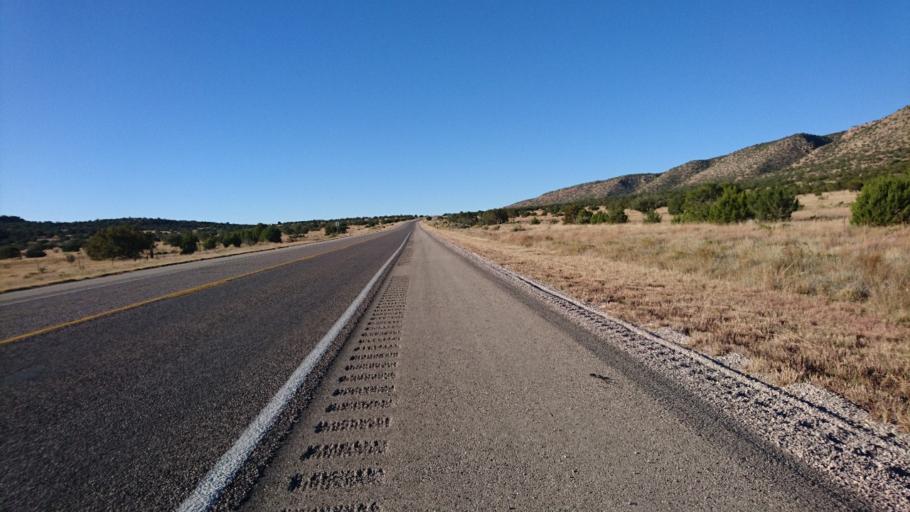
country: US
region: New Mexico
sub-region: Cibola County
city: Grants
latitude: 35.0105
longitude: -107.8900
